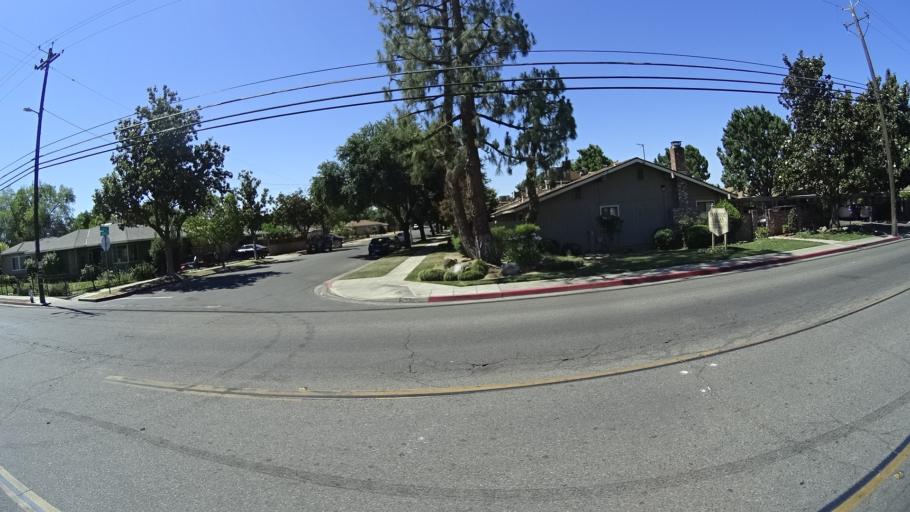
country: US
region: California
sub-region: Fresno County
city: Fresno
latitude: 36.7866
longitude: -119.8219
